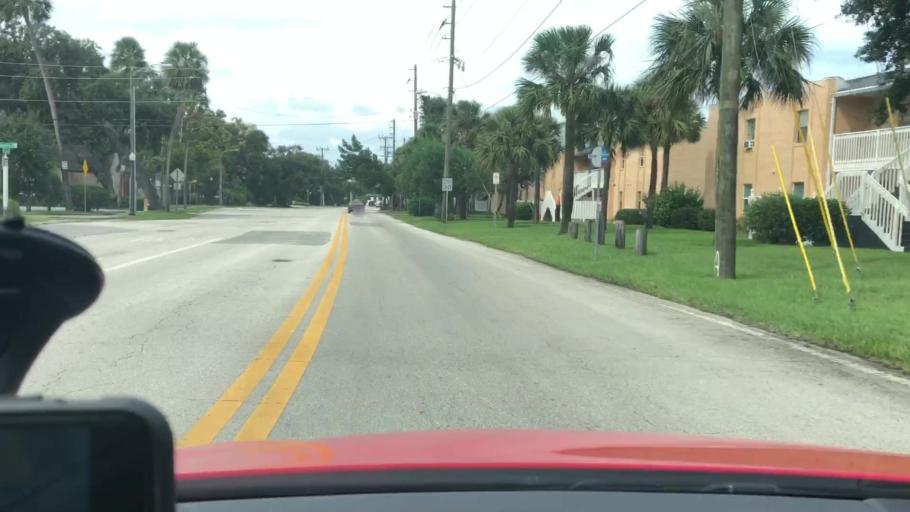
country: US
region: Florida
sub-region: Volusia County
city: Daytona Beach
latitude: 29.1987
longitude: -81.0134
